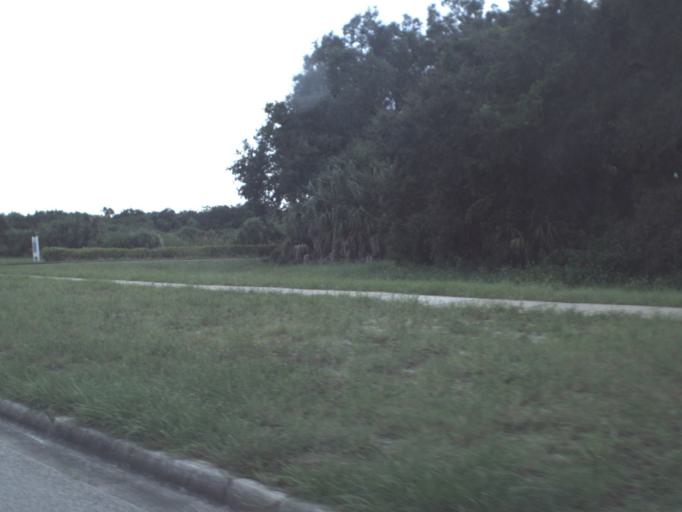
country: US
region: Florida
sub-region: Pinellas County
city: Tierra Verde
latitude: 27.6675
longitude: -82.7258
